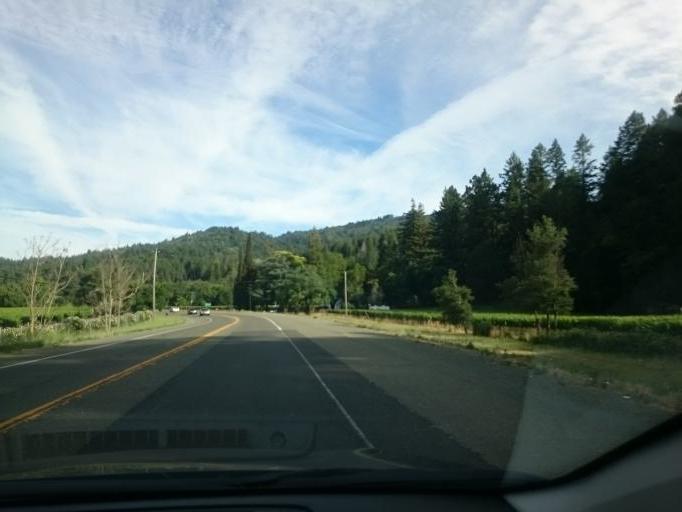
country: US
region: California
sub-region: Napa County
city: Calistoga
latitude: 38.5684
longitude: -122.5661
